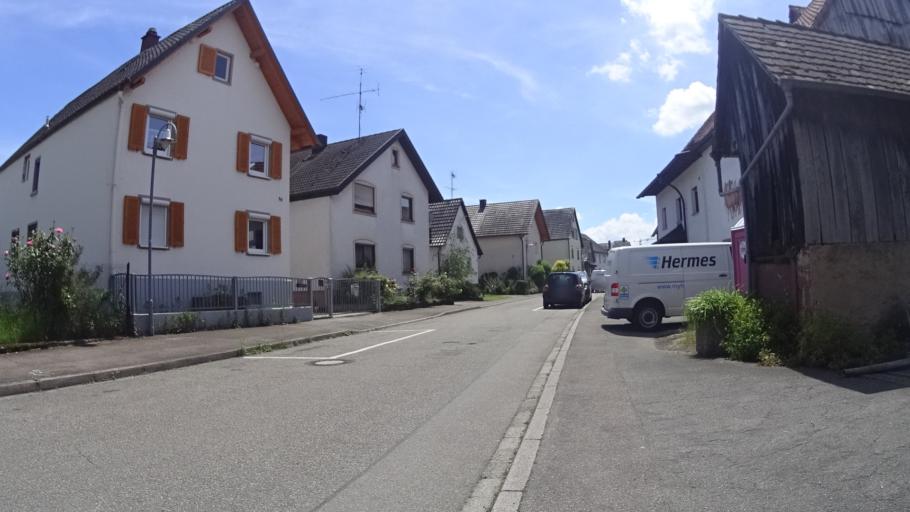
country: DE
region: Baden-Wuerttemberg
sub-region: Freiburg Region
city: Kappel-Grafenhausen
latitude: 48.2960
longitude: 7.7439
